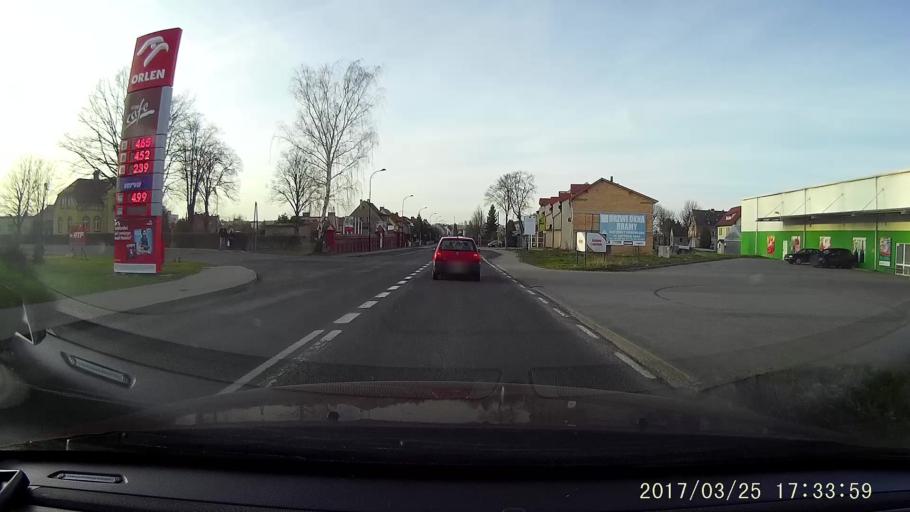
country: PL
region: Lower Silesian Voivodeship
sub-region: Powiat zgorzelecki
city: Zgorzelec
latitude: 51.1276
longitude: 15.0160
